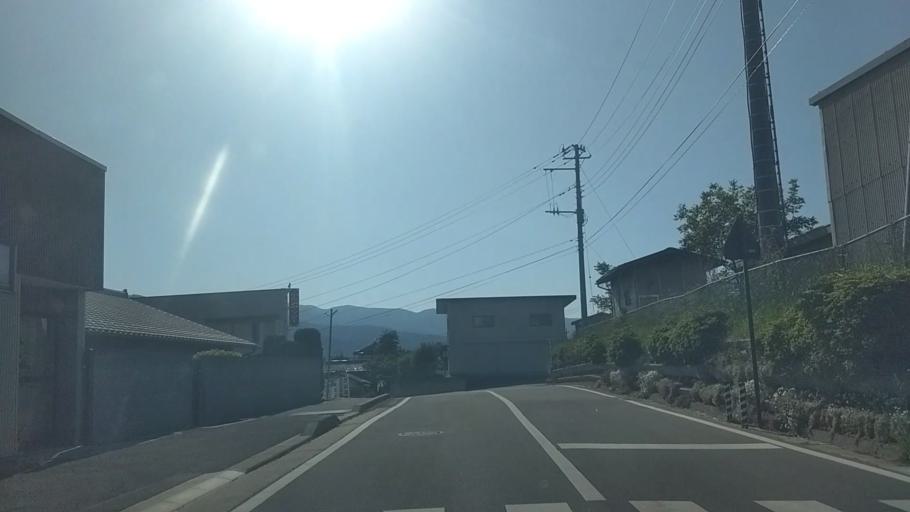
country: JP
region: Nagano
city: Chino
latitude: 35.8638
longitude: 138.3151
